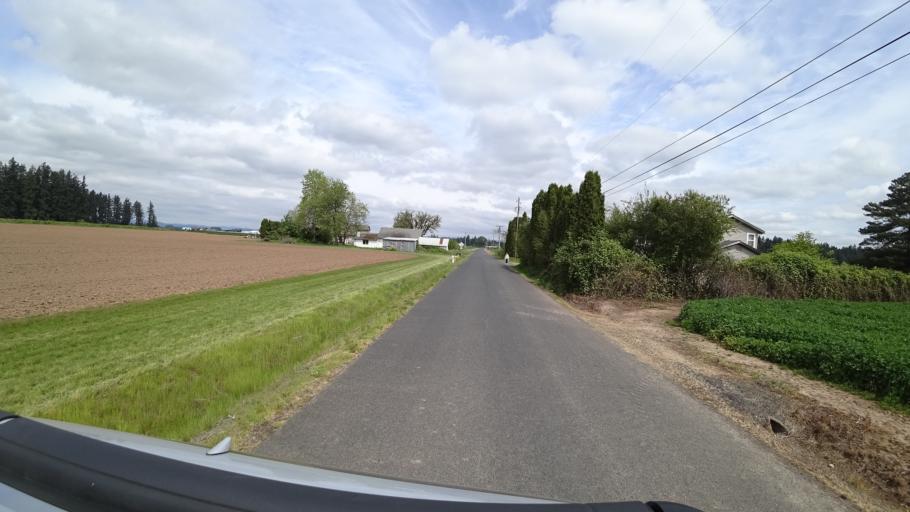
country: US
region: Oregon
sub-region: Washington County
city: Hillsboro
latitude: 45.5335
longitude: -123.0108
